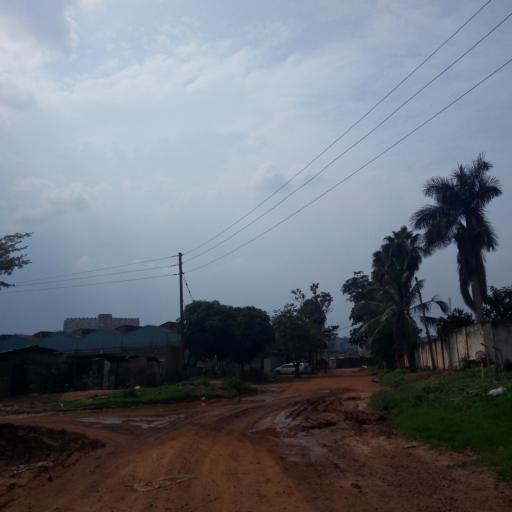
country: UG
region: Central Region
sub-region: Kampala District
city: Kampala
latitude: 0.3157
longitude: 32.6156
